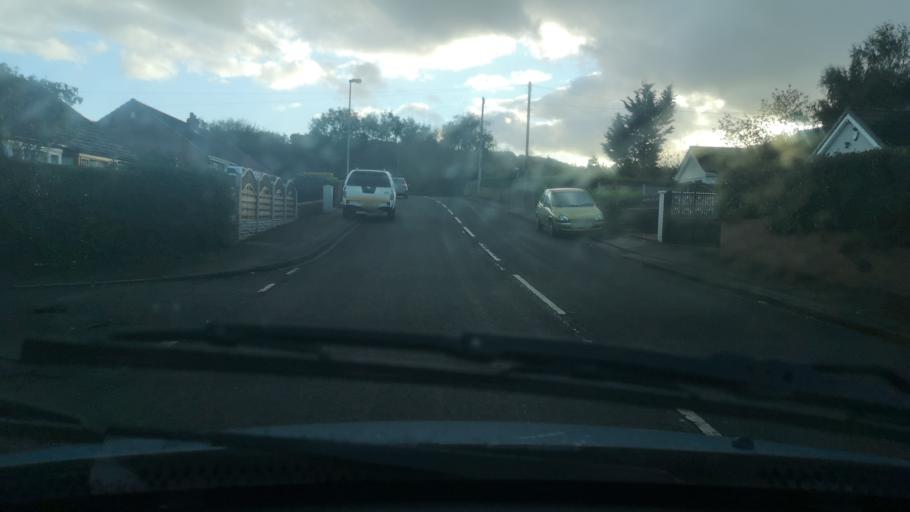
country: GB
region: England
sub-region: City and Borough of Wakefield
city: Crigglestone
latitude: 53.6297
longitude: -1.5254
